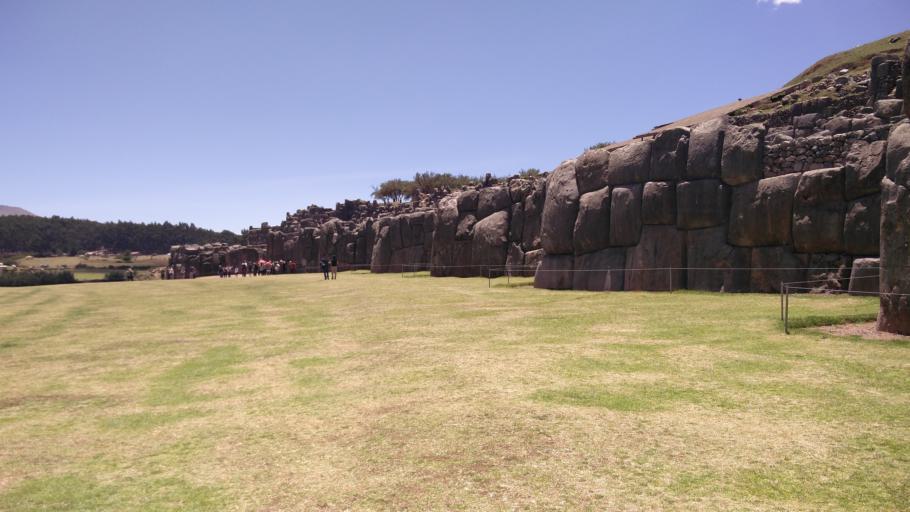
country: PE
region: Cusco
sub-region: Provincia de Cusco
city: Cusco
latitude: -13.5082
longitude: -71.9828
